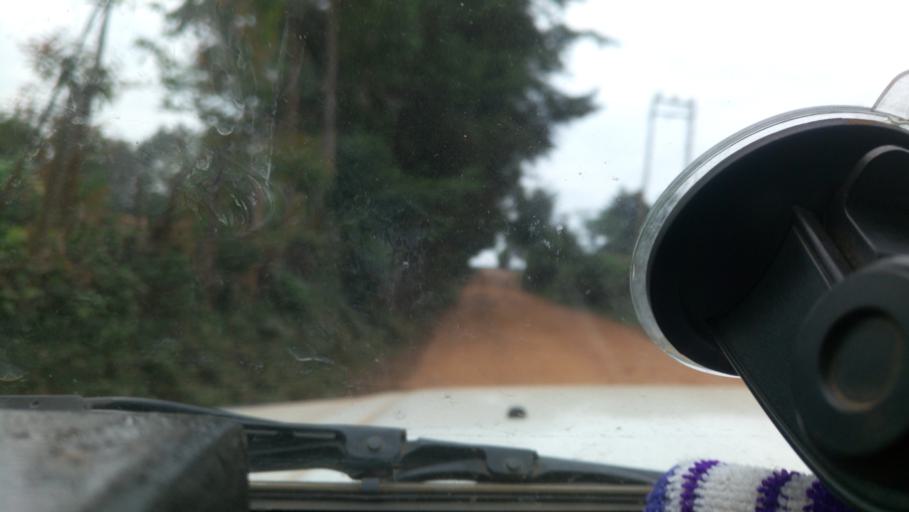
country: KE
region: Kericho
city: Litein
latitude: -0.5974
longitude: 35.2239
